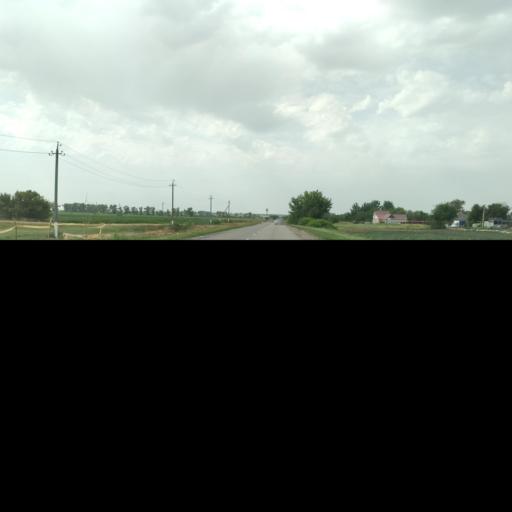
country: RU
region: Voronezj
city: Davydovka
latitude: 51.2271
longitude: 39.5319
